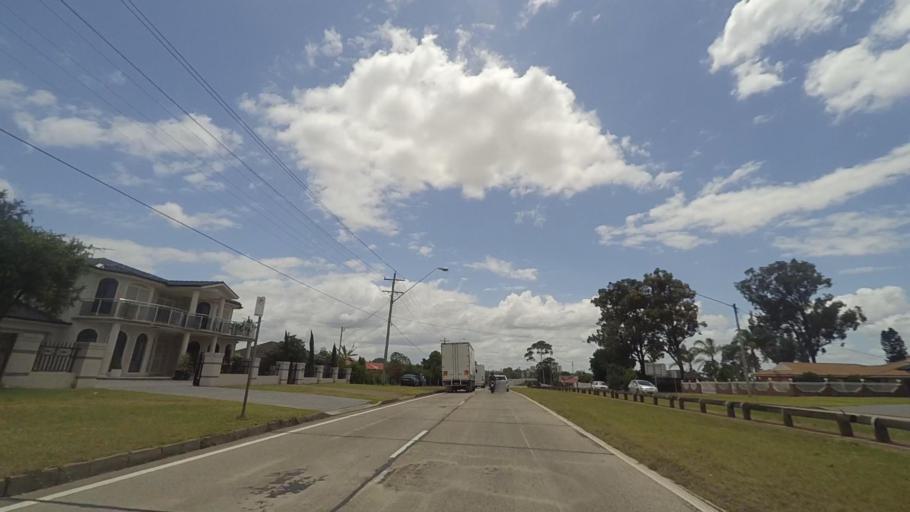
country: AU
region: New South Wales
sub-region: Fairfield
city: Fairfield Heights
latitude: -33.8652
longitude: 150.9260
